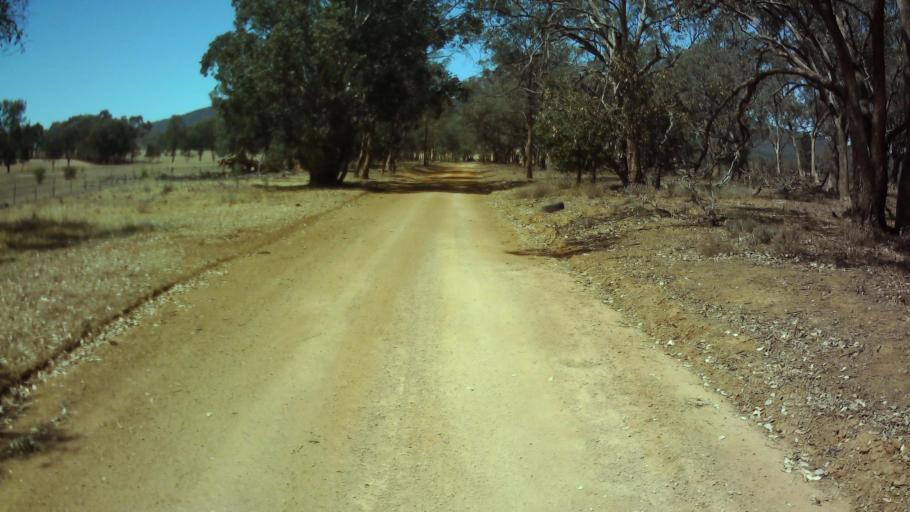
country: AU
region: New South Wales
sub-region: Weddin
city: Grenfell
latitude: -33.9533
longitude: 148.0846
